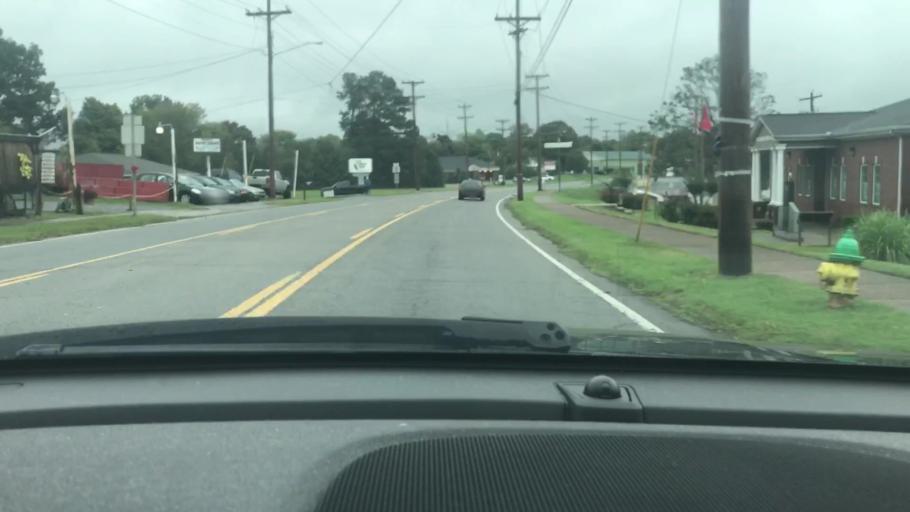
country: US
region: Tennessee
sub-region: Dickson County
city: White Bluff
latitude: 36.1084
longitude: -87.2253
